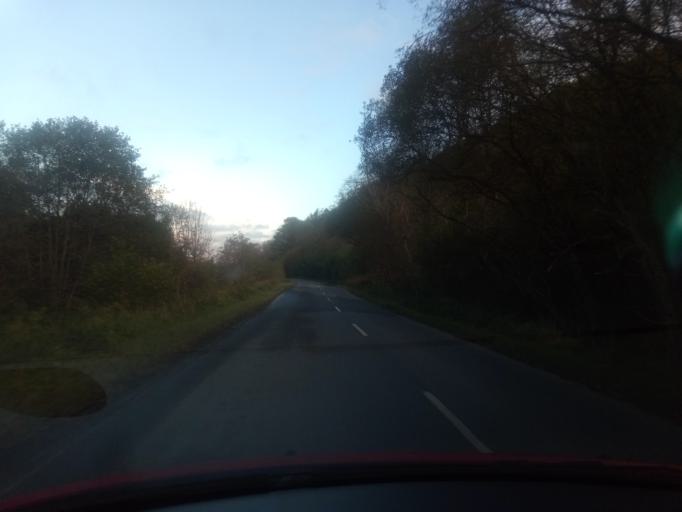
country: GB
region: Scotland
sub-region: The Scottish Borders
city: Hawick
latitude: 55.3567
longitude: -2.6482
